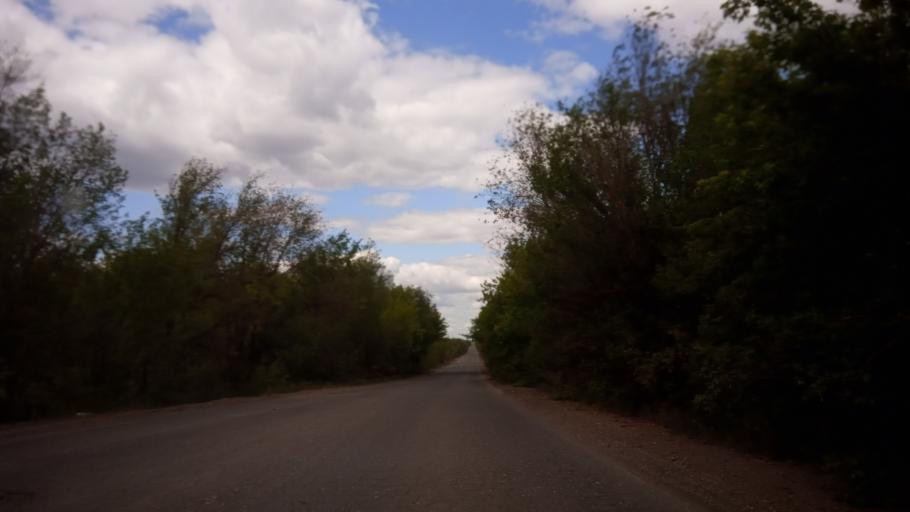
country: RU
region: Orenburg
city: Novotroitsk
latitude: 51.2416
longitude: 58.3556
